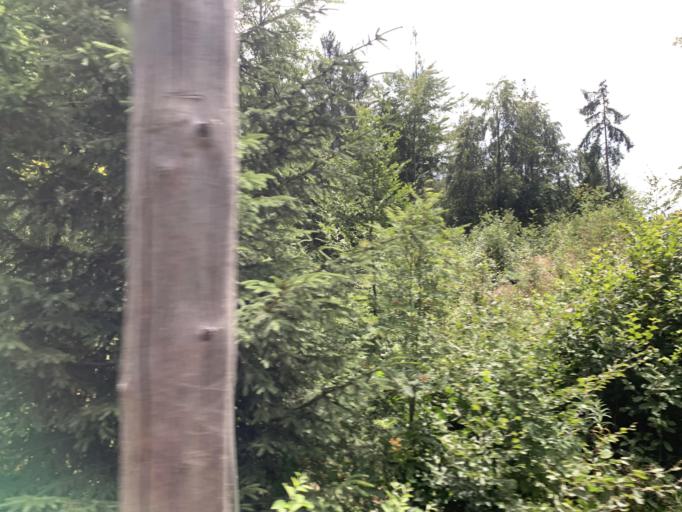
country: IT
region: Trentino-Alto Adige
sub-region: Bolzano
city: Soprabolzano
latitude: 46.5256
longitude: 11.4312
